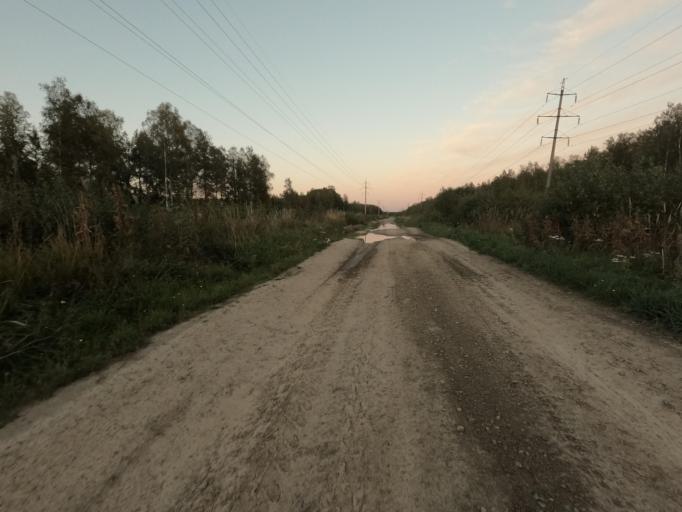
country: RU
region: Leningrad
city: Otradnoye
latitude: 59.7696
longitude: 30.8430
